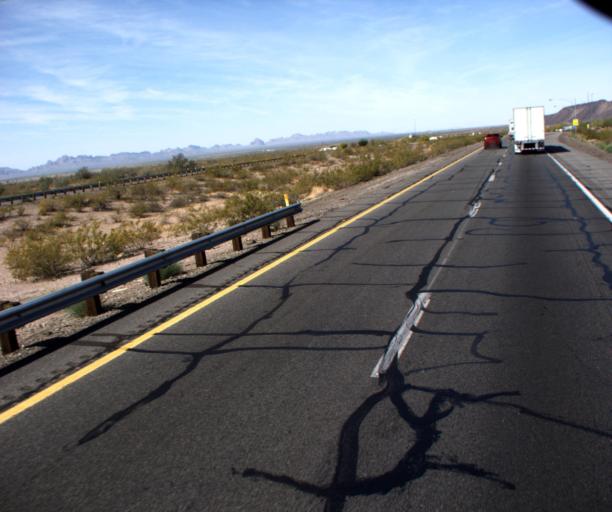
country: US
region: Arizona
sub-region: Maricopa County
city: Buckeye
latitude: 33.5195
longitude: -113.0613
